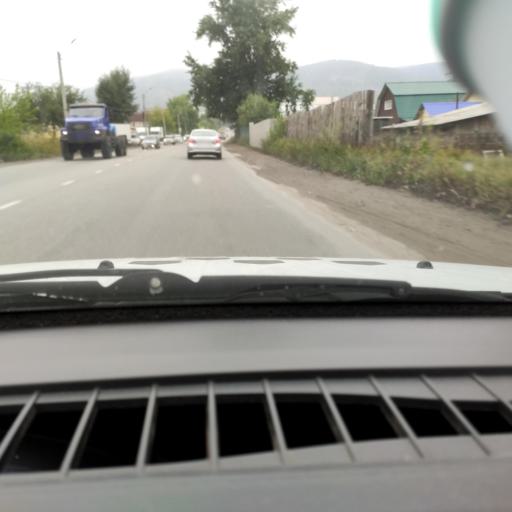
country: RU
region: Chelyabinsk
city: Miass
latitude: 55.0262
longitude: 60.1113
